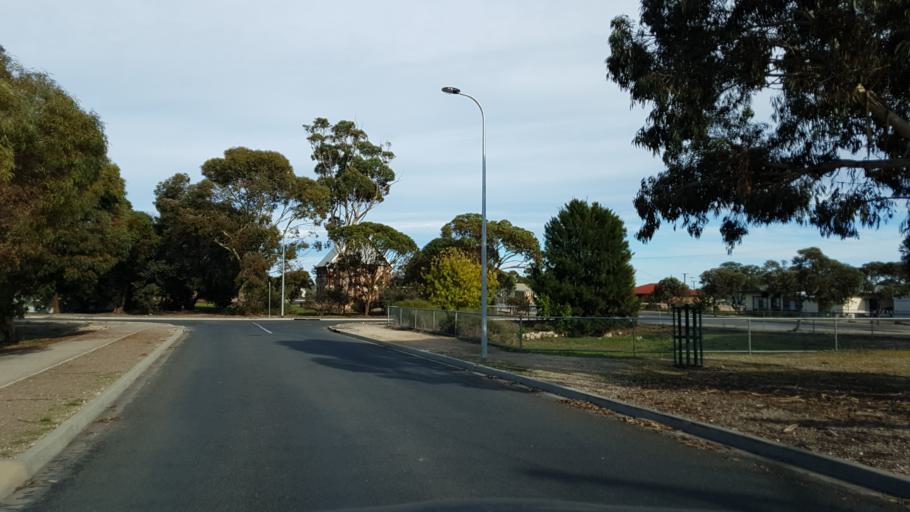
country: AU
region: South Australia
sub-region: Murray Bridge
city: Tailem Bend
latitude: -35.2517
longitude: 139.4560
